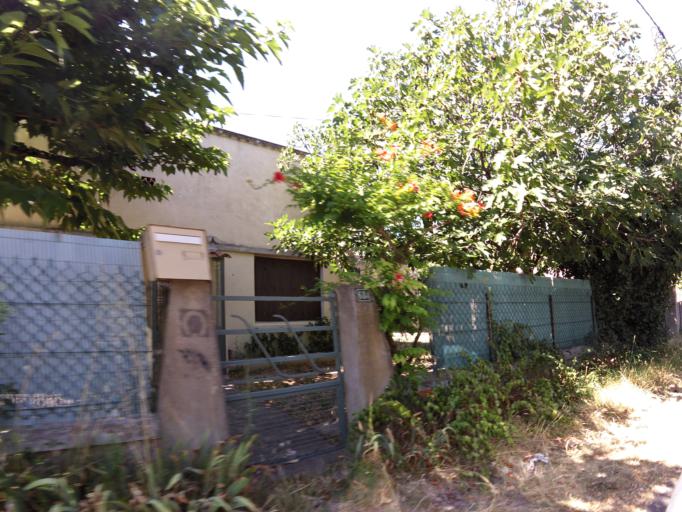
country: FR
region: Languedoc-Roussillon
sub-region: Departement de l'Herault
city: Boisseron
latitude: 43.7625
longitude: 4.0503
